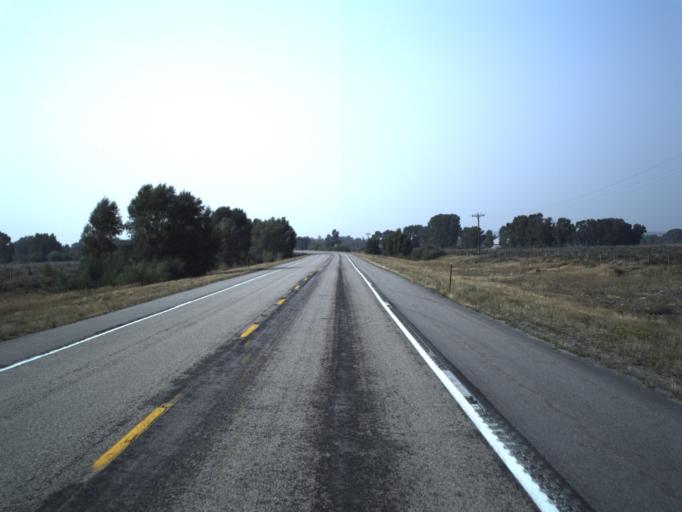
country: US
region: Wyoming
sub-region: Uinta County
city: Evanston
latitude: 40.9987
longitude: -110.8656
